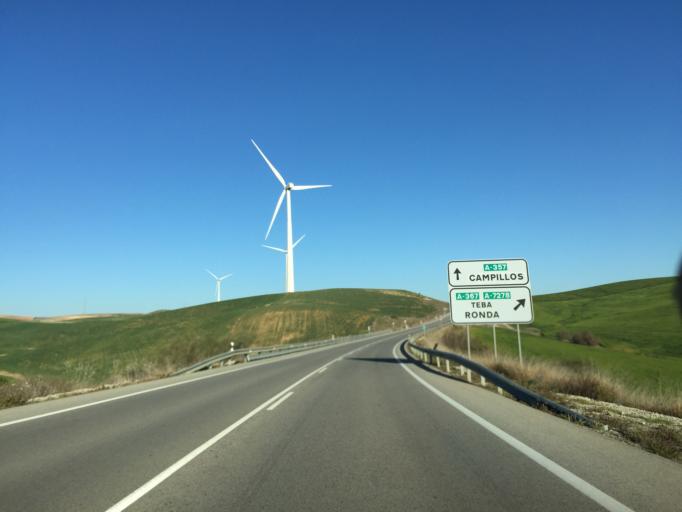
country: ES
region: Andalusia
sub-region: Provincia de Malaga
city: Ardales
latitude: 36.9325
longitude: -4.8601
